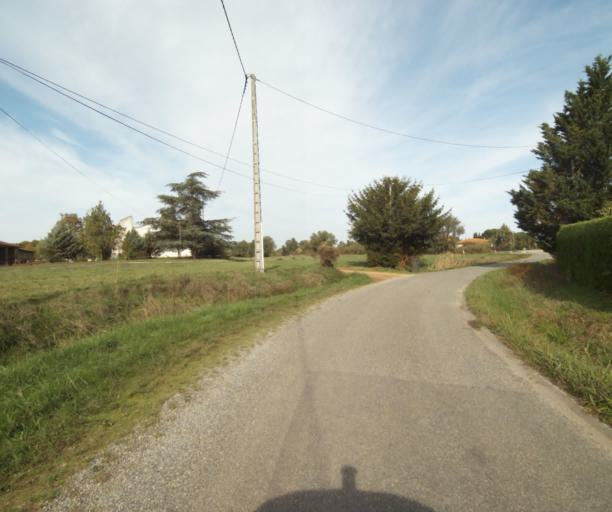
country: FR
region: Midi-Pyrenees
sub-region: Departement du Tarn-et-Garonne
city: Orgueil
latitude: 43.9009
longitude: 1.4104
